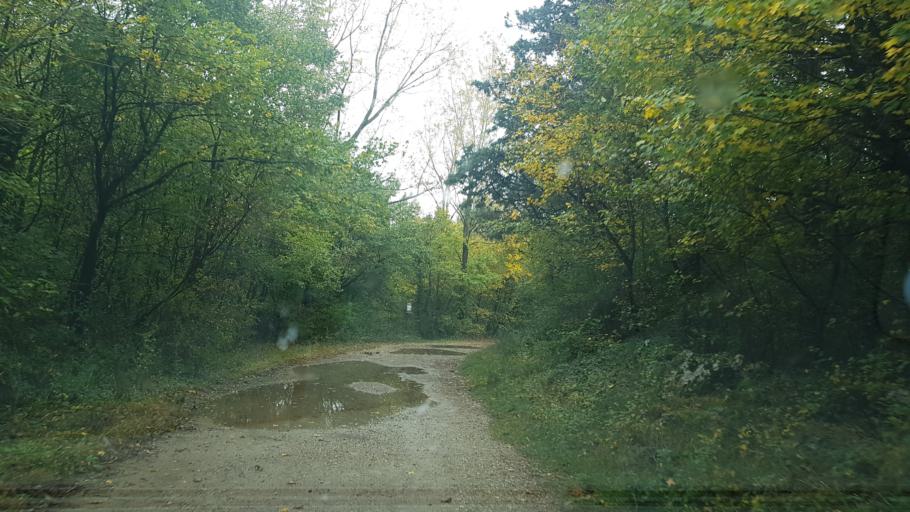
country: IT
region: Friuli Venezia Giulia
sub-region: Provincia di Gorizia
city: Monfalcone
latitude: 45.8181
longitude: 13.5283
